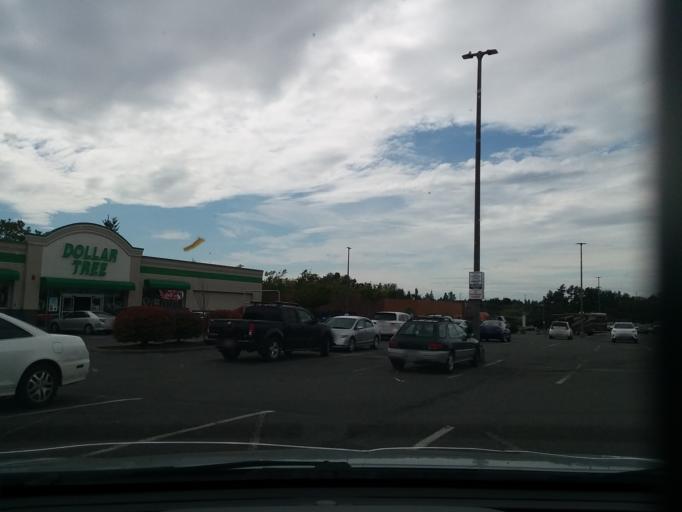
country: US
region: Washington
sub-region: Whatcom County
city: Bellingham
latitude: 48.7851
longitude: -122.4824
